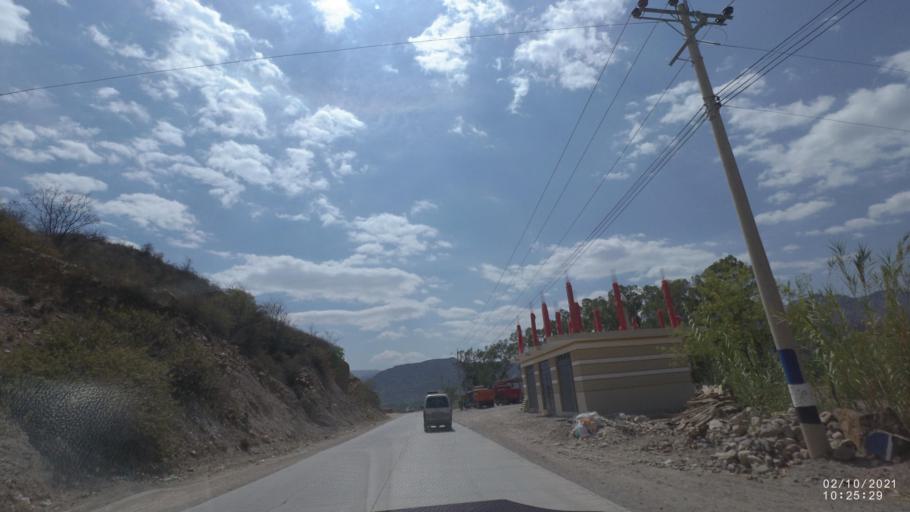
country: BO
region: Cochabamba
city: Irpa Irpa
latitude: -17.7239
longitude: -66.2677
